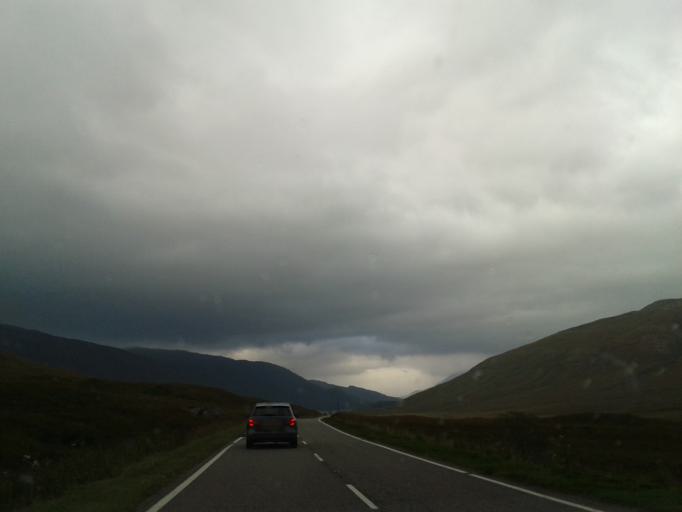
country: GB
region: Scotland
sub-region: Highland
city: Fort William
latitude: 57.1530
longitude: -5.2112
